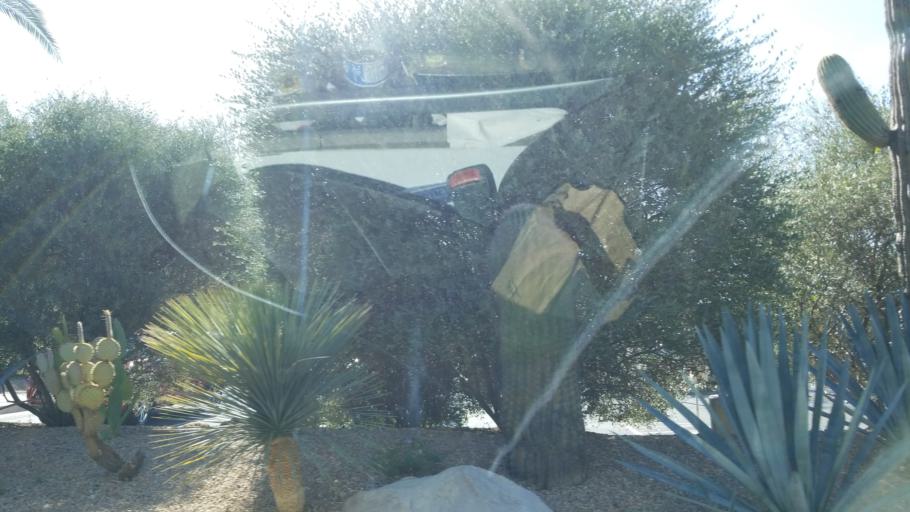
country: US
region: Arizona
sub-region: Maricopa County
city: Paradise Valley
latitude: 33.5666
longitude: -111.9191
